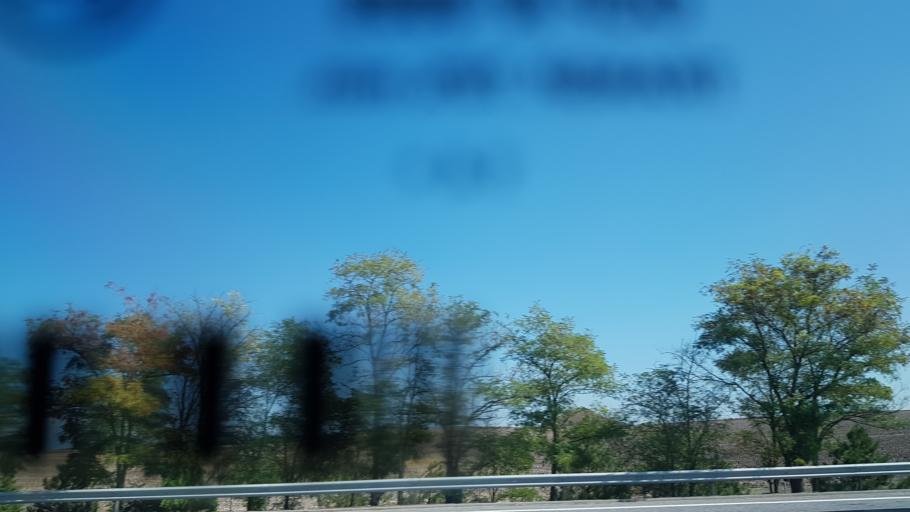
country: TR
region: Kirklareli
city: Luleburgaz
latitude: 41.4135
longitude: 27.3868
